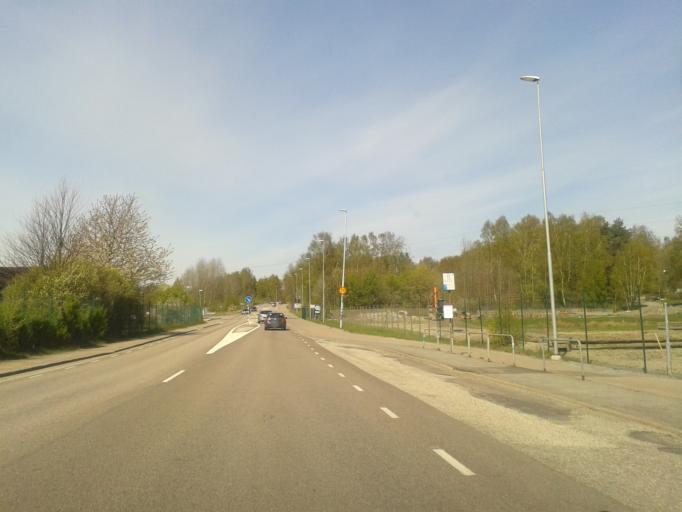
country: SE
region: Vaestra Goetaland
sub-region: Goteborg
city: Eriksbo
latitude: 57.7558
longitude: 12.0110
